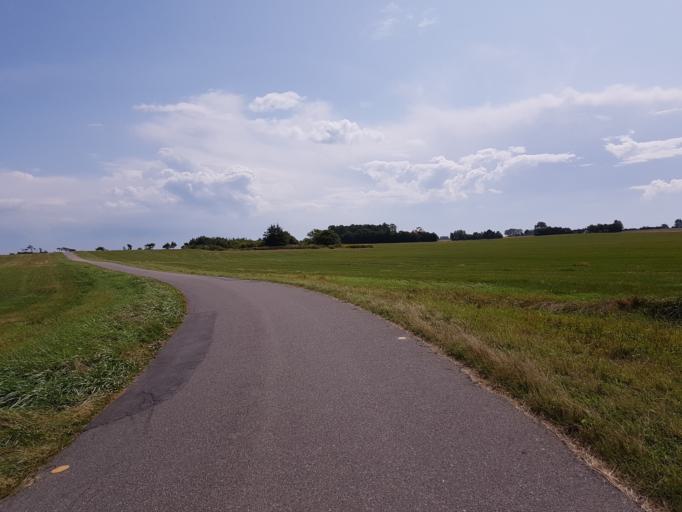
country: DK
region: Zealand
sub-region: Guldborgsund Kommune
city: Nykobing Falster
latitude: 54.5805
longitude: 11.9603
